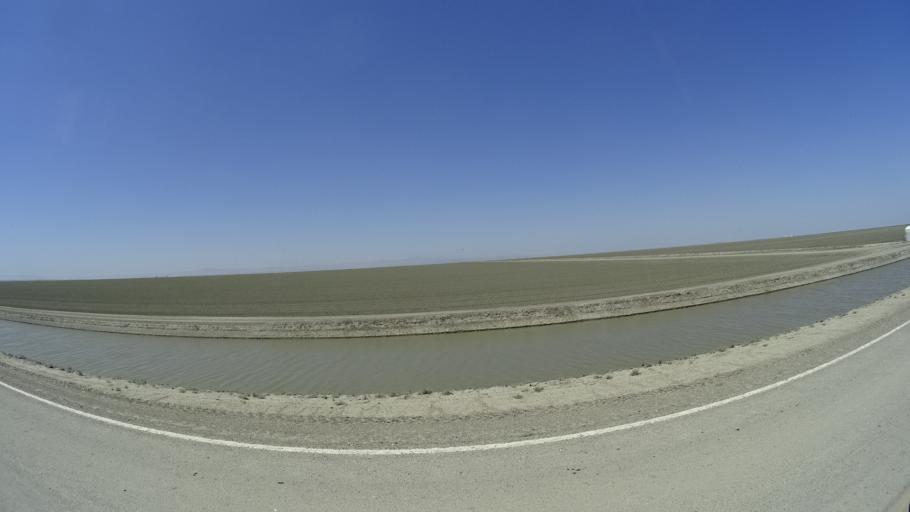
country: US
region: California
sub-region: Kings County
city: Corcoran
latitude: 35.9771
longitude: -119.6431
